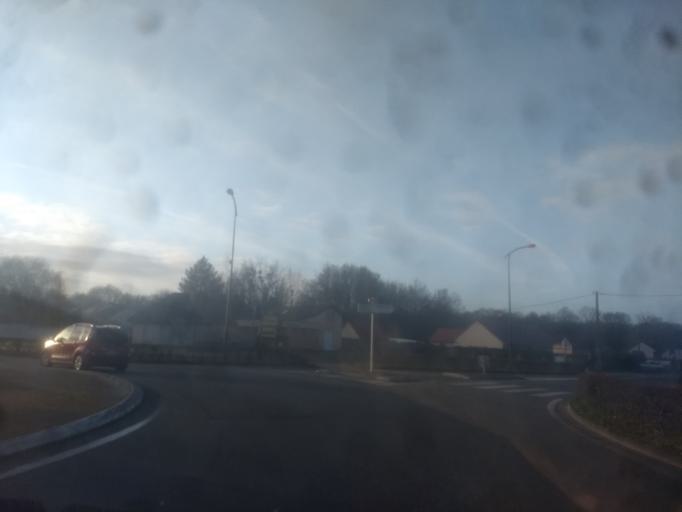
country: FR
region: Centre
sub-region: Departement du Cher
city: Vignoux-sur-Barangeon
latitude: 47.1943
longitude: 2.1776
